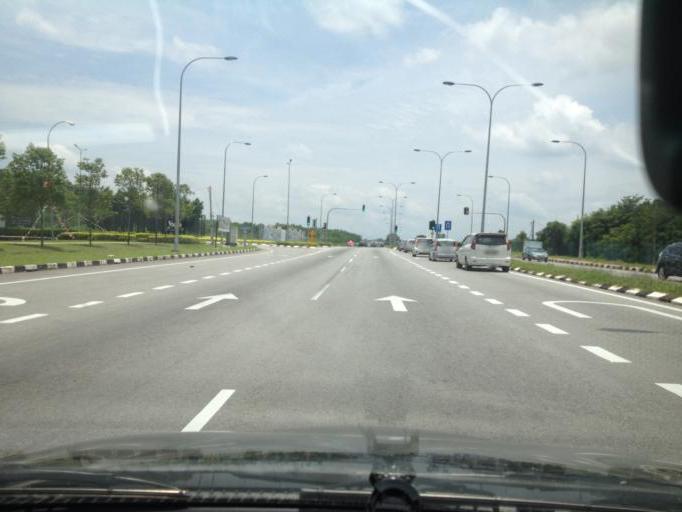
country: MY
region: Kedah
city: Sungai Petani
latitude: 5.6207
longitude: 100.5400
